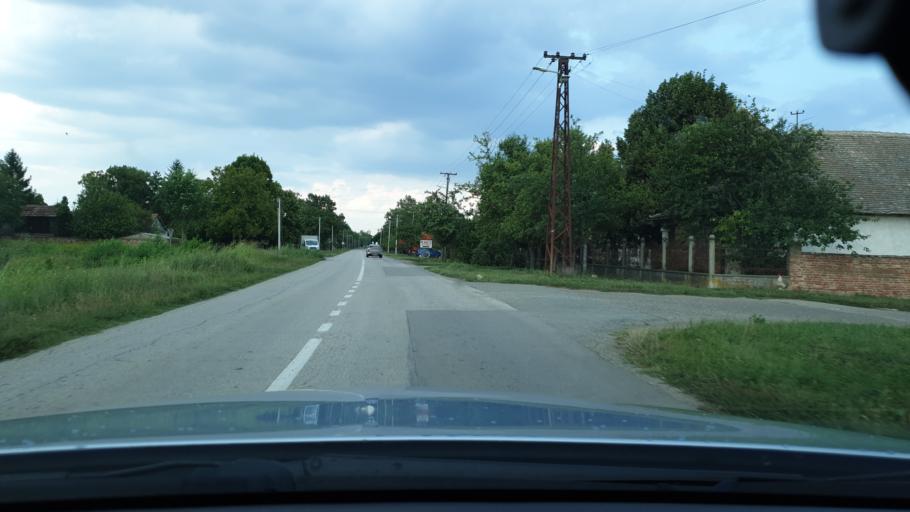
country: RS
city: Boka
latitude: 45.3485
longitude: 20.8273
